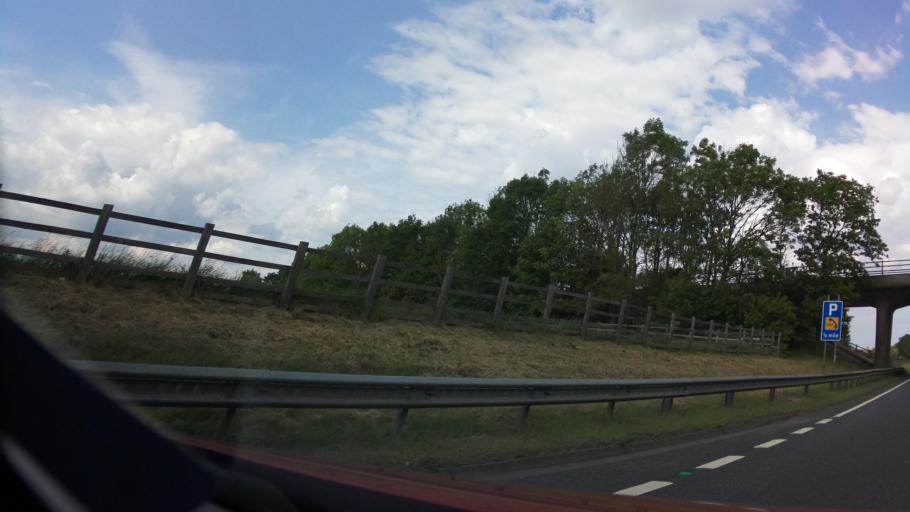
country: GB
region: England
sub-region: Redcar and Cleveland
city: Thornaby-on-Tees
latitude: 54.4983
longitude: -1.2947
